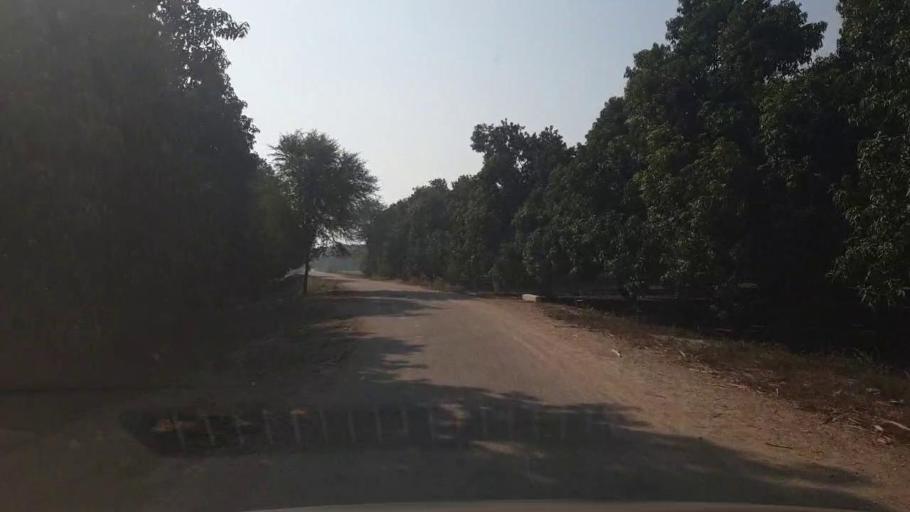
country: PK
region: Sindh
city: Tando Allahyar
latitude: 25.4698
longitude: 68.7627
